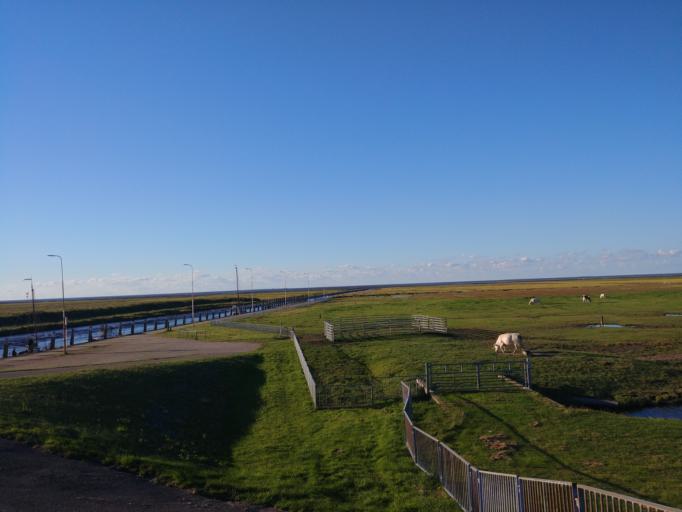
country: NL
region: Groningen
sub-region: Gemeente Winsum
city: Winsum
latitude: 53.4333
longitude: 6.5831
